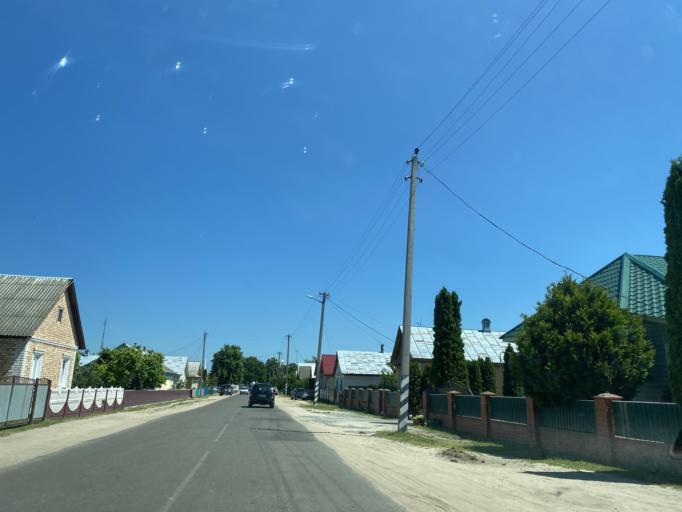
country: BY
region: Brest
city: Ivanava
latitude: 52.3160
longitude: 25.6028
